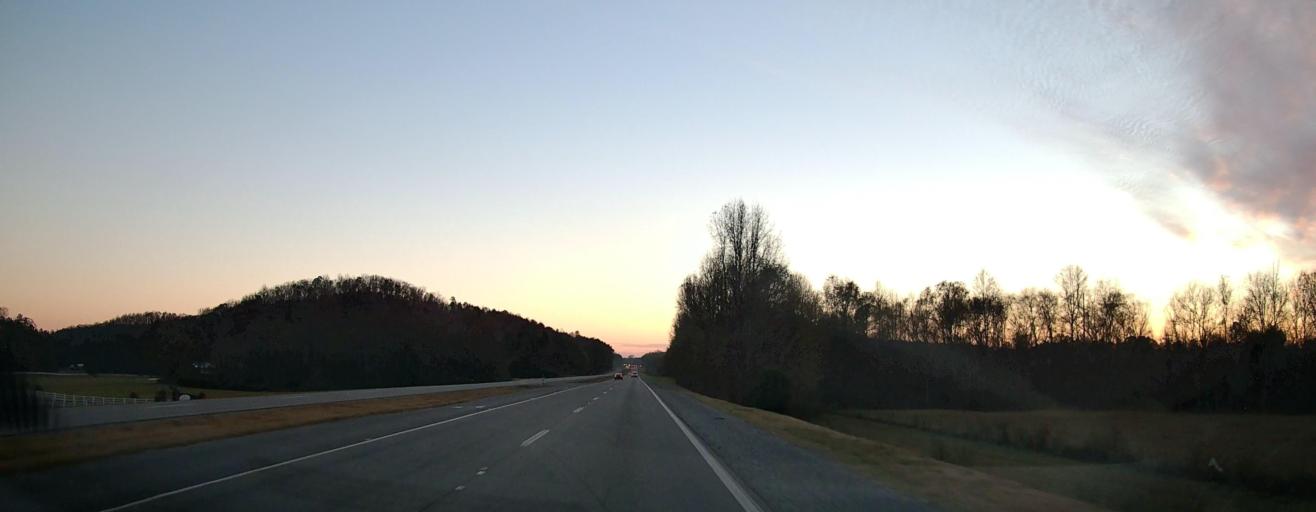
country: US
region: Alabama
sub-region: Etowah County
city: Glencoe
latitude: 33.8639
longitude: -85.9156
